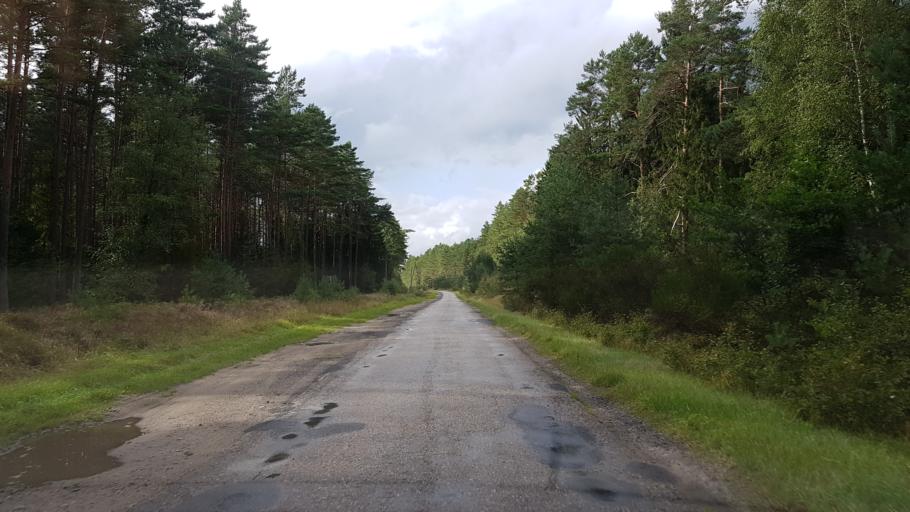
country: PL
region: West Pomeranian Voivodeship
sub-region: Powiat bialogardzki
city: Tychowo
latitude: 54.0386
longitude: 16.3313
